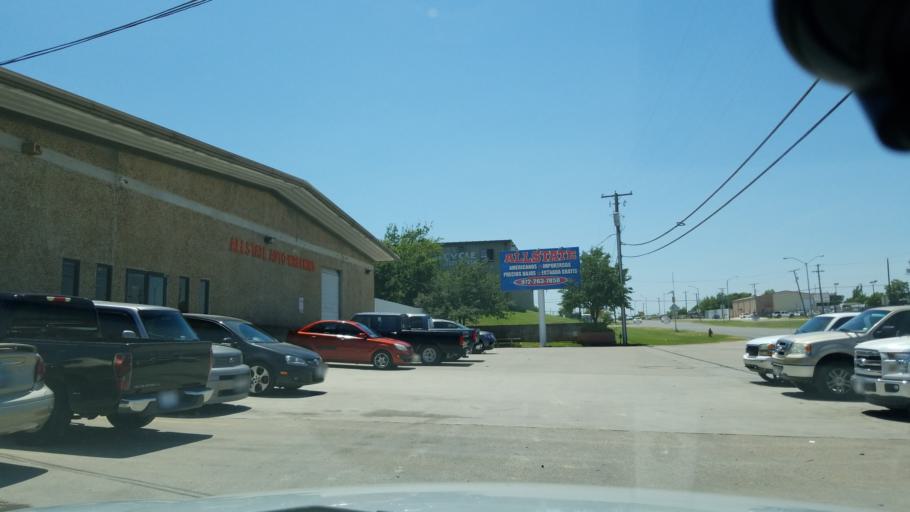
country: US
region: Texas
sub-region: Dallas County
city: Grand Prairie
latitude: 32.7461
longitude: -96.9516
